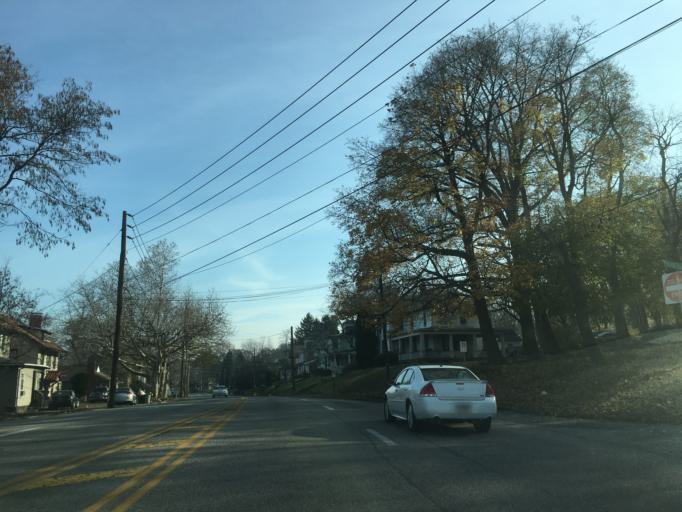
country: US
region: Pennsylvania
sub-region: Dauphin County
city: Penbrook
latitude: 40.2740
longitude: -76.8593
